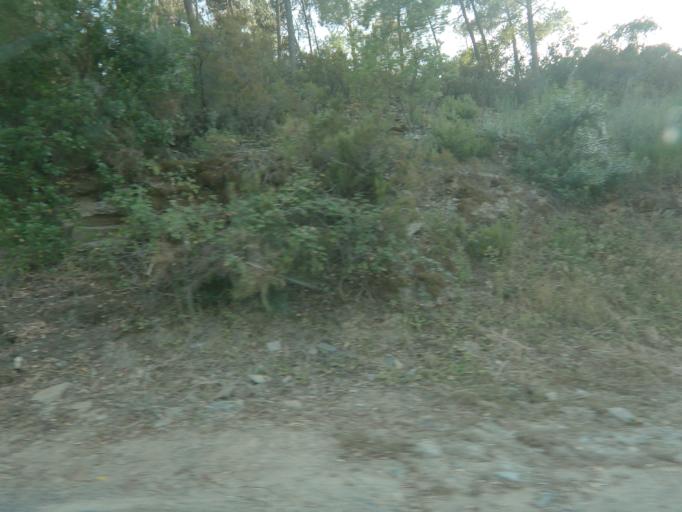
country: PT
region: Vila Real
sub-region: Sabrosa
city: Vilela
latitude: 41.1752
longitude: -7.5900
